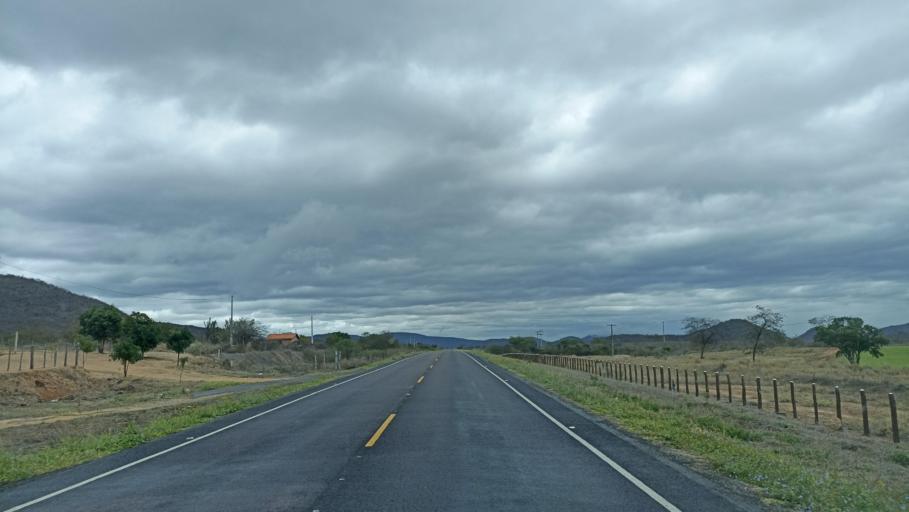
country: BR
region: Bahia
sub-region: Iacu
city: Iacu
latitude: -12.8957
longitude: -40.3993
